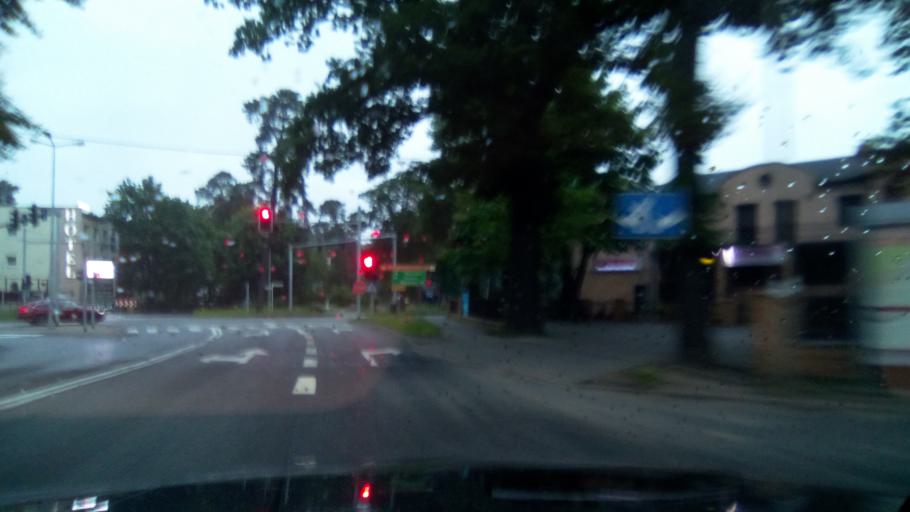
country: PL
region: Greater Poland Voivodeship
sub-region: Powiat poznanski
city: Kobylnica
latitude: 52.4458
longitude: 17.0766
